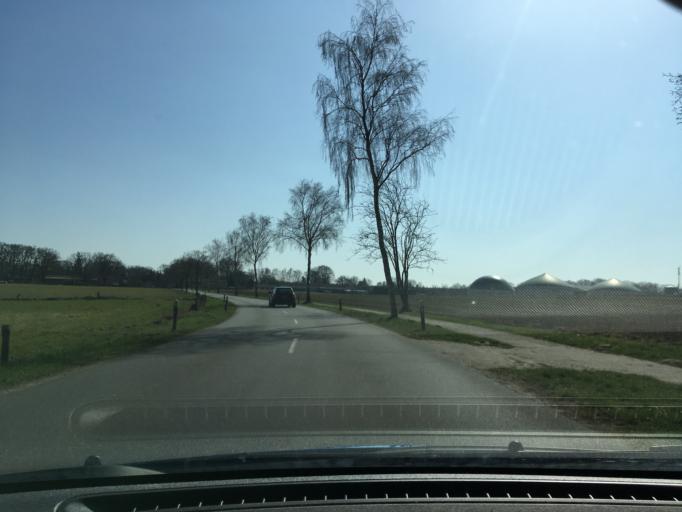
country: DE
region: Lower Saxony
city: Eimke
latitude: 52.9711
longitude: 10.3128
